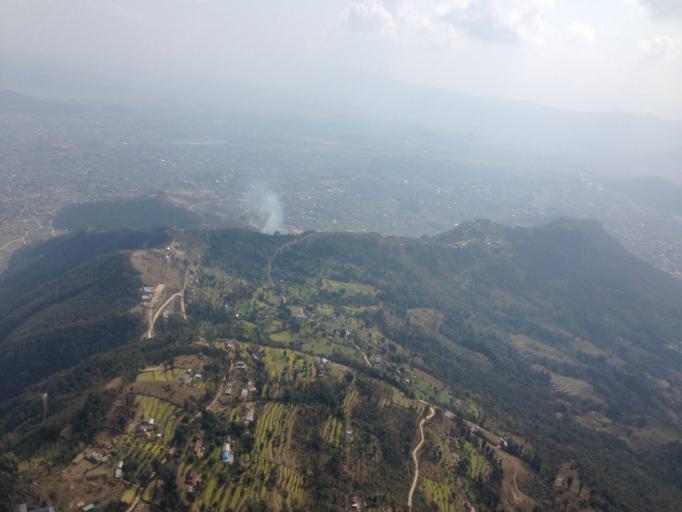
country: NP
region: Western Region
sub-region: Gandaki Zone
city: Pokhara
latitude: 28.2453
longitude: 83.9576
